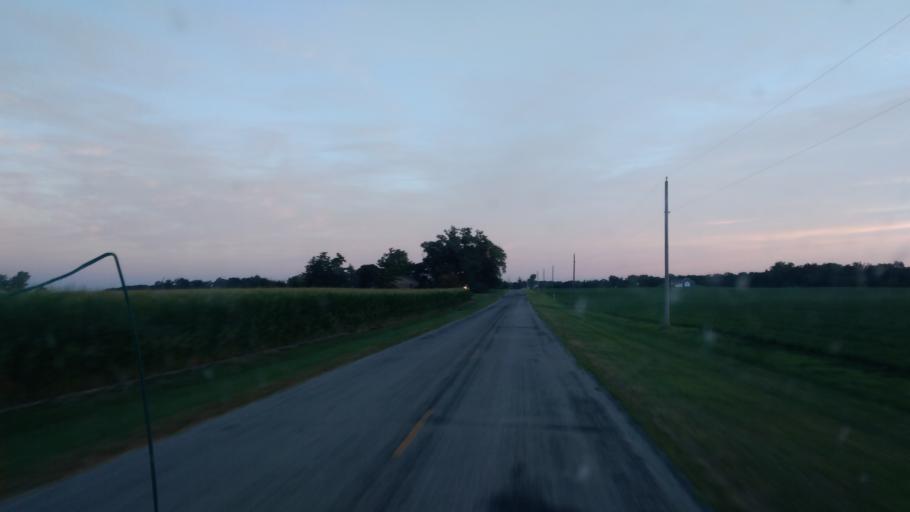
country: US
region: Indiana
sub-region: Wells County
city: Bluffton
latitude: 40.6760
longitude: -85.1308
